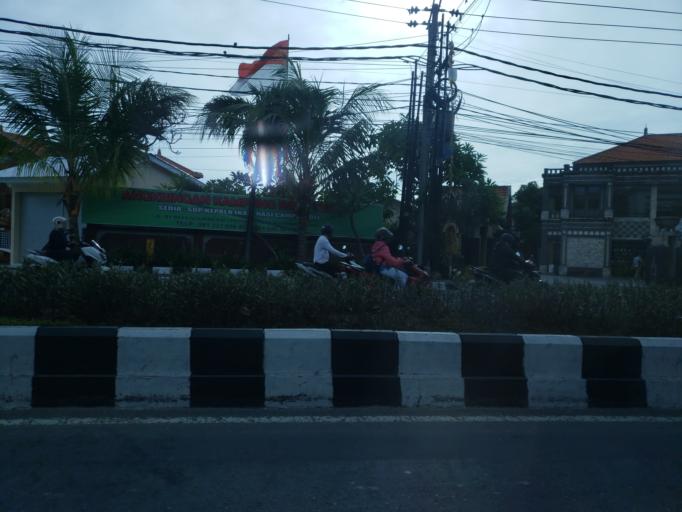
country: ID
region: Bali
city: Kelanabian
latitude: -8.7418
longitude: 115.1812
